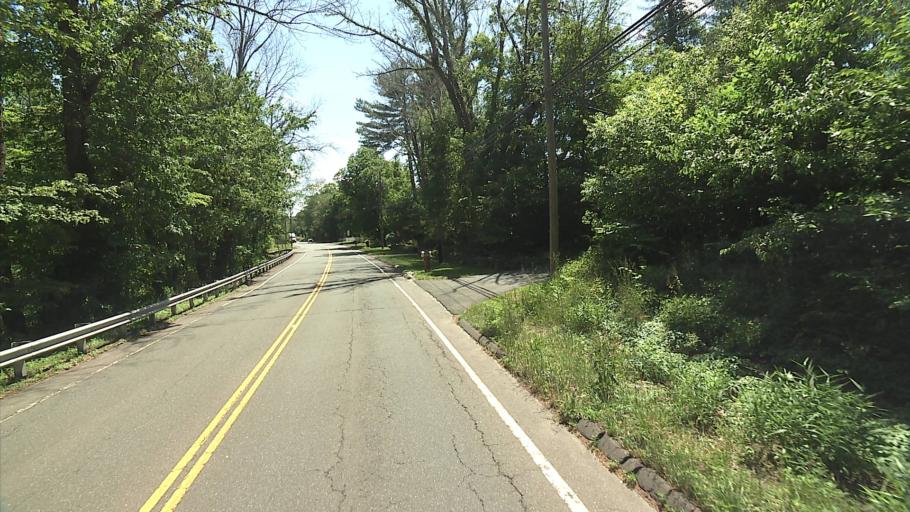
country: US
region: Connecticut
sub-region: New Haven County
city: Woodbridge
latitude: 41.3811
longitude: -73.0016
